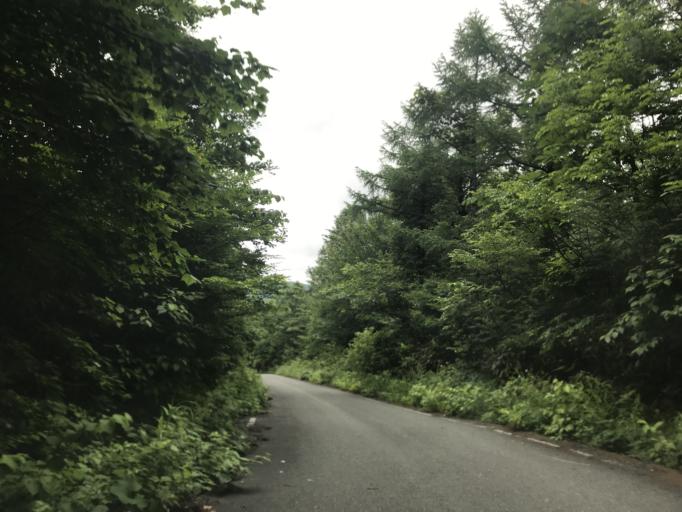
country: JP
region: Iwate
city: Ichinoseki
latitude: 38.9401
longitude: 140.8767
